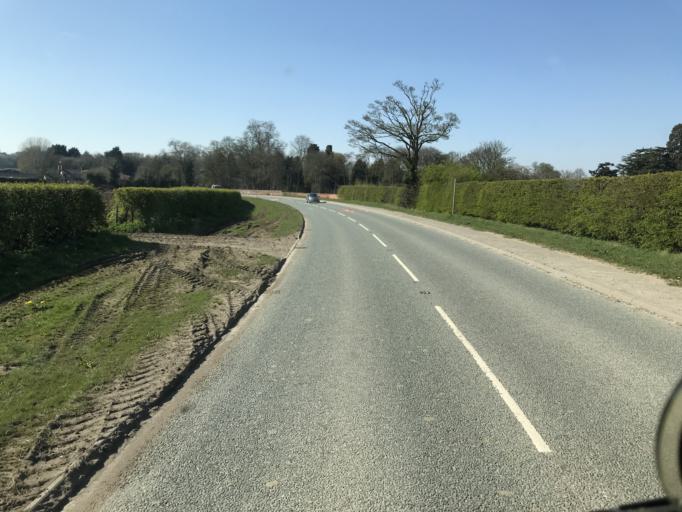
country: GB
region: Wales
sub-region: Wrexham
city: Rossett
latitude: 53.1064
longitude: -2.9613
